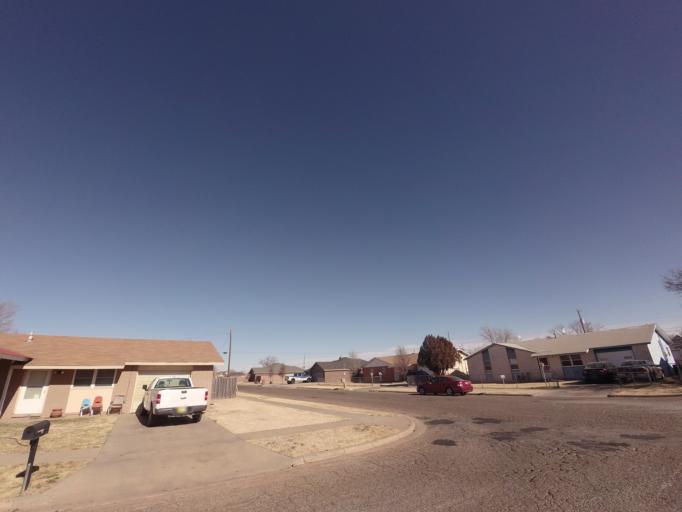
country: US
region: New Mexico
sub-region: Curry County
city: Clovis
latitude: 34.4095
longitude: -103.2284
